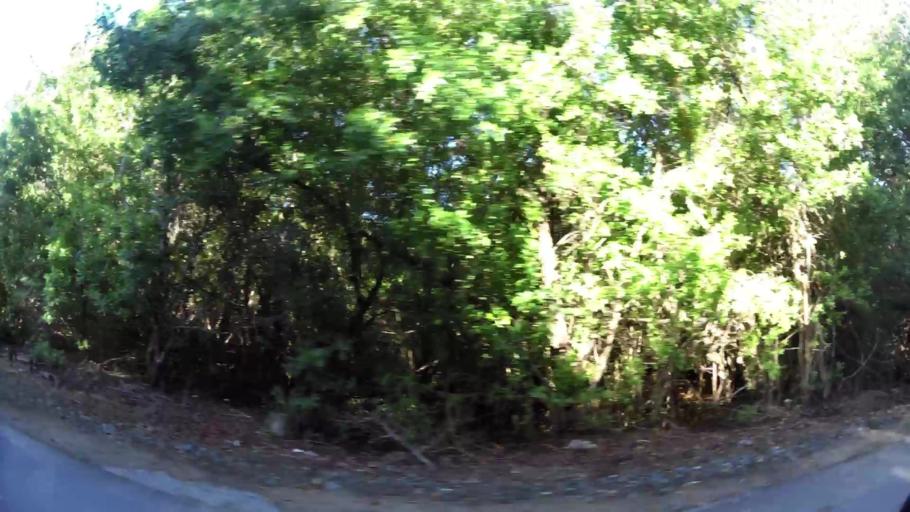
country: TT
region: Tobago
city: Scarborough
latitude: 11.1488
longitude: -60.8141
